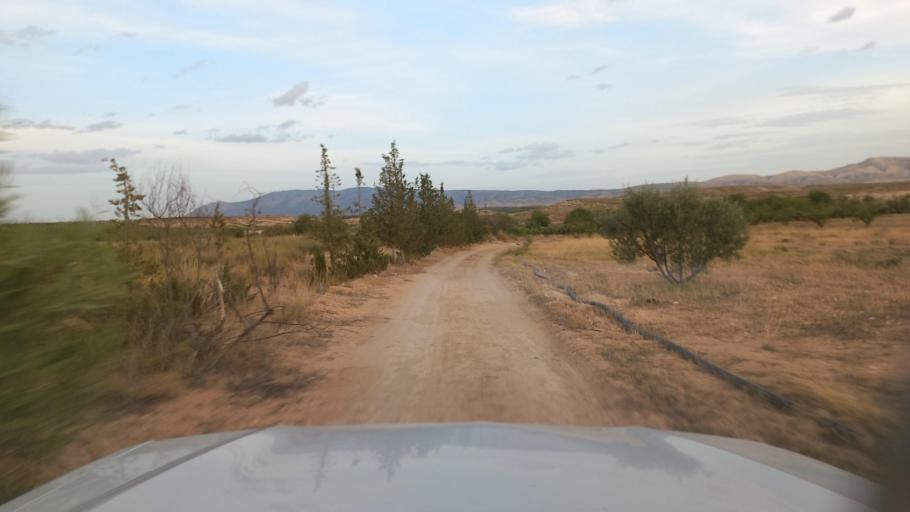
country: TN
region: Al Qasrayn
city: Sbiba
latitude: 35.4100
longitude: 9.0845
